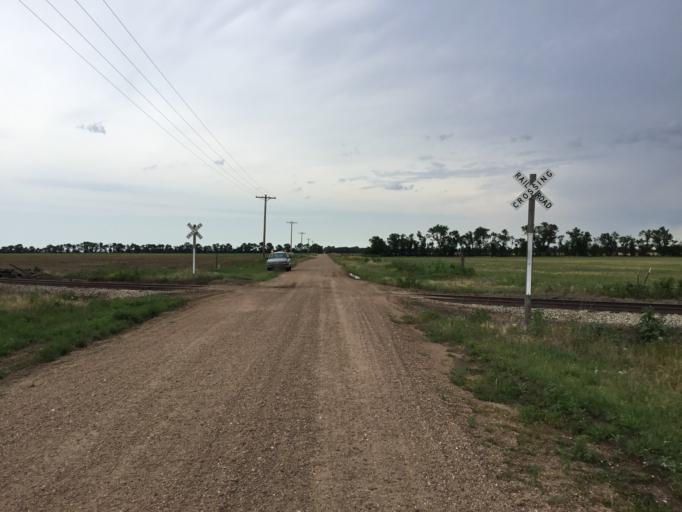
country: US
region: Kansas
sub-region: Sumner County
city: Conway Springs
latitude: 37.4425
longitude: -97.8257
